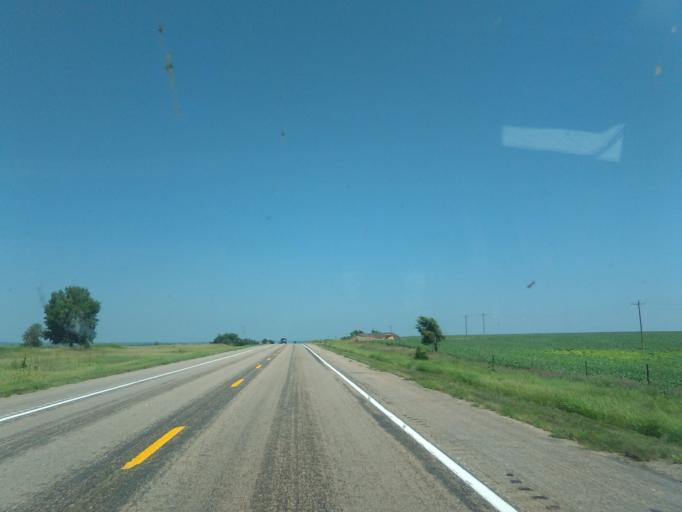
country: US
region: Nebraska
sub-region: Frontier County
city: Stockville
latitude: 40.6013
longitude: -100.6296
